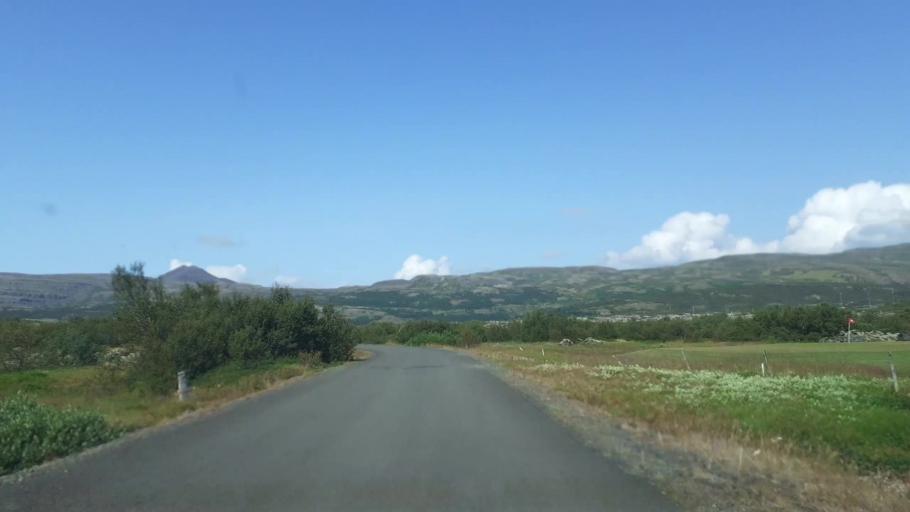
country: IS
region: West
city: Borgarnes
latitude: 64.7563
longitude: -21.5512
